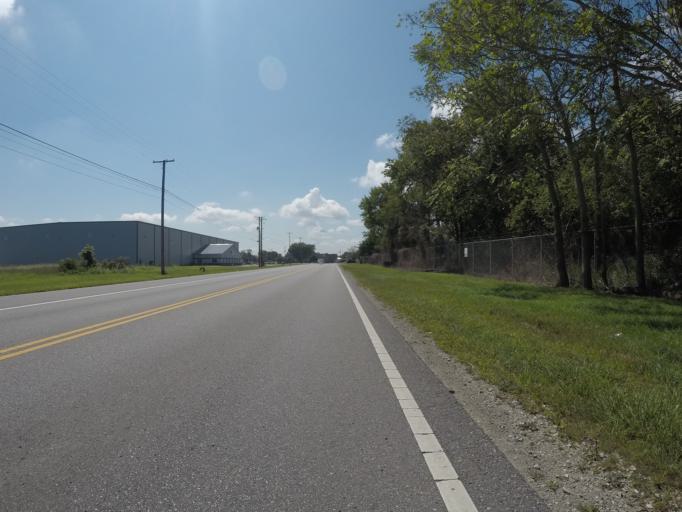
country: US
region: Ohio
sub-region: Lawrence County
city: South Point
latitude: 38.4356
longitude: -82.5949
